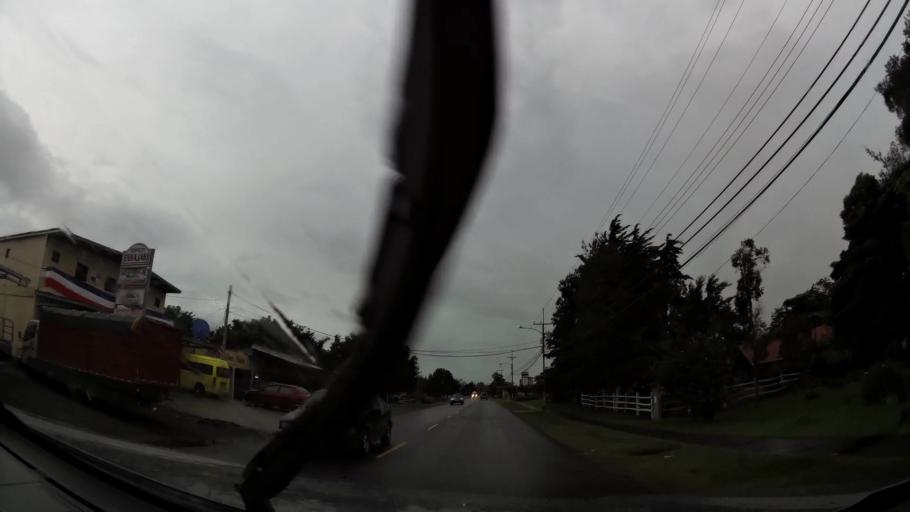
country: PA
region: Chiriqui
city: Volcan
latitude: 8.7857
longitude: -82.6506
